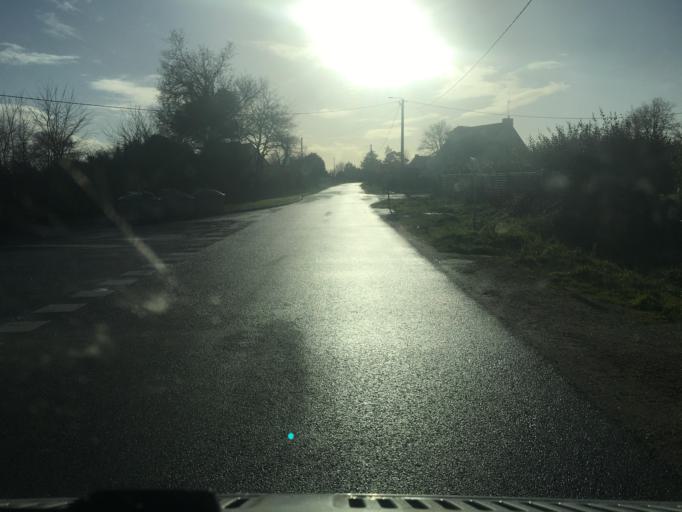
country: FR
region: Brittany
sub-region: Departement du Morbihan
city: Surzur
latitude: 47.5181
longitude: -2.6718
